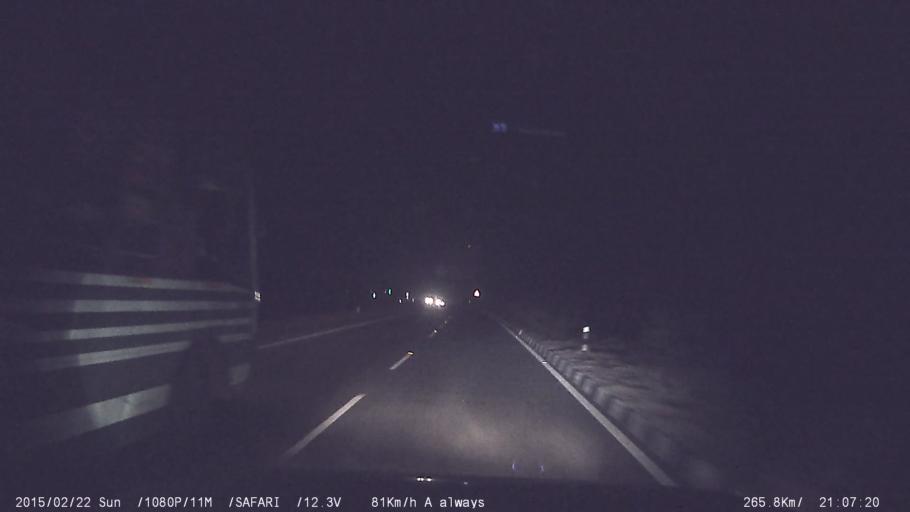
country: IN
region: Tamil Nadu
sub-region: Karur
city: Pallappatti
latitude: 10.7210
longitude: 77.9285
